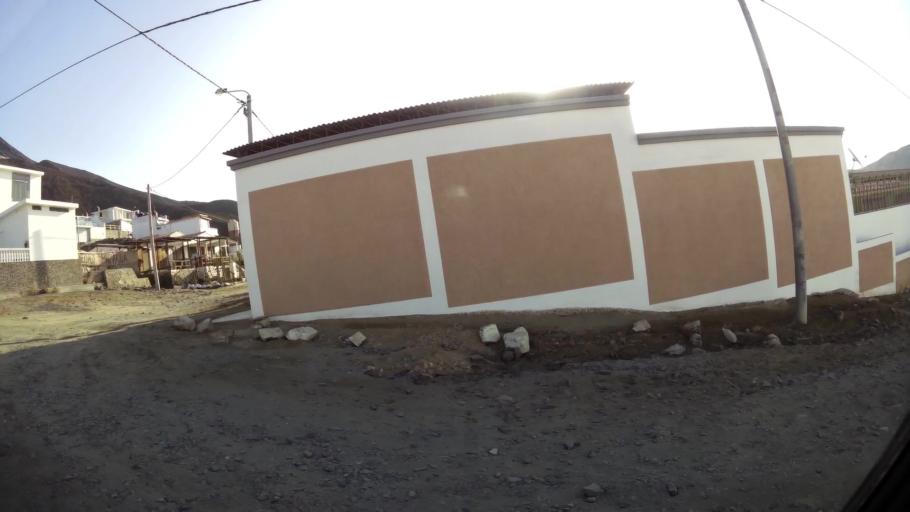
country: PE
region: Ancash
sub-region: Provincia de Casma
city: Puerto Casma
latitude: -9.3692
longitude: -78.4154
